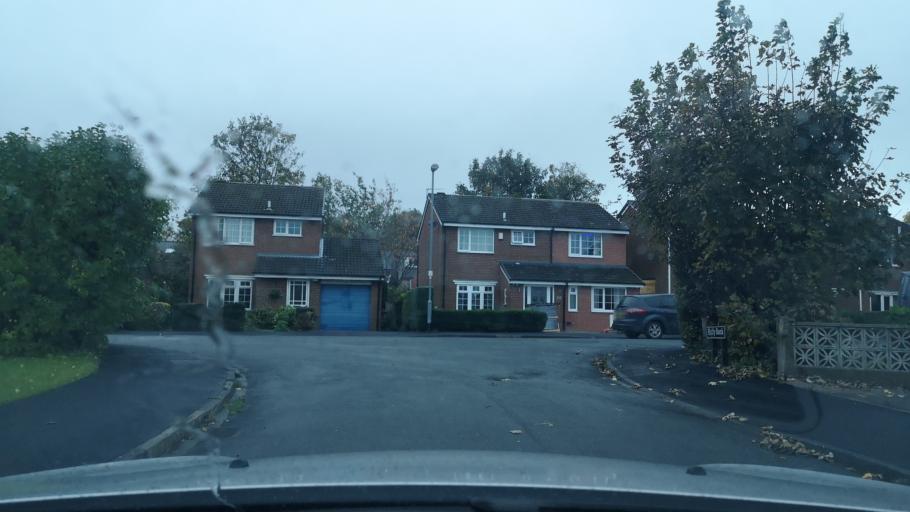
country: GB
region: England
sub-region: City and Borough of Wakefield
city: Low Ackworth
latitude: 53.6454
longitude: -1.3457
